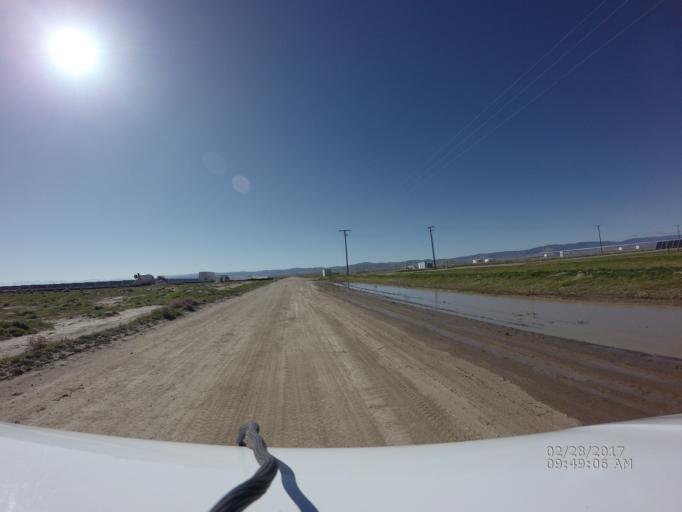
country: US
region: California
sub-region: Los Angeles County
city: Green Valley
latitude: 34.8127
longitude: -118.3614
